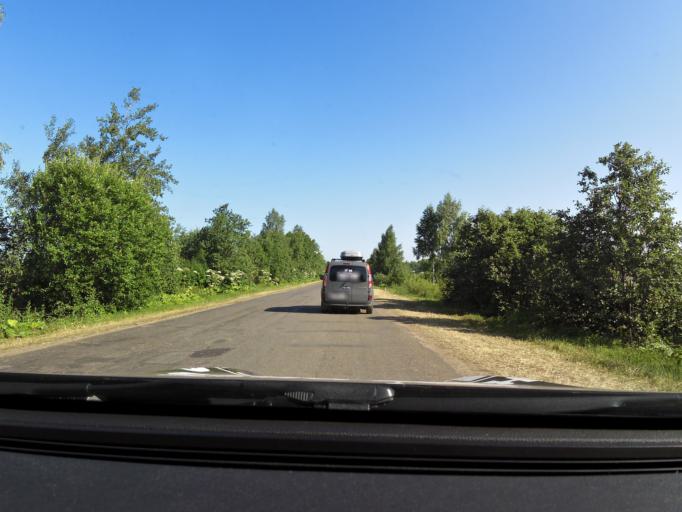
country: RU
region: Tverskaya
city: Zavidovo
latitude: 56.6073
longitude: 36.6376
